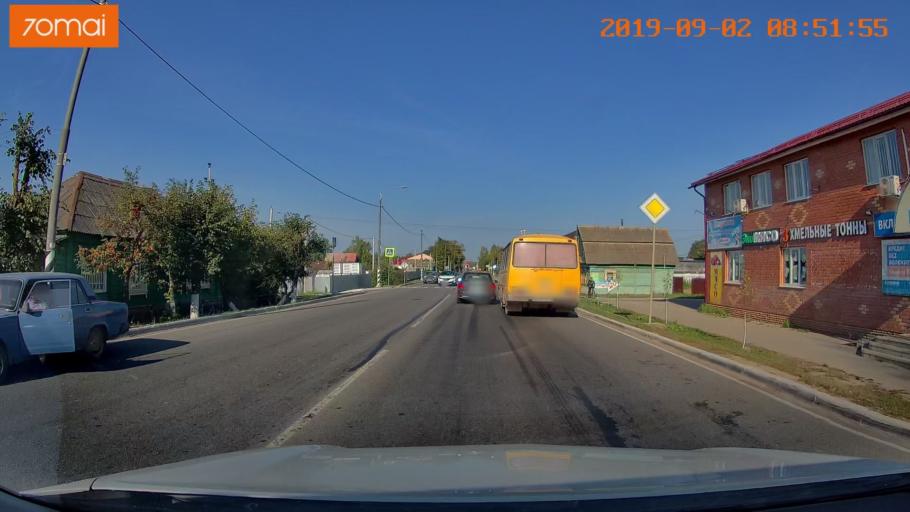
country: RU
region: Kaluga
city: Medyn'
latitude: 54.9660
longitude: 35.8690
